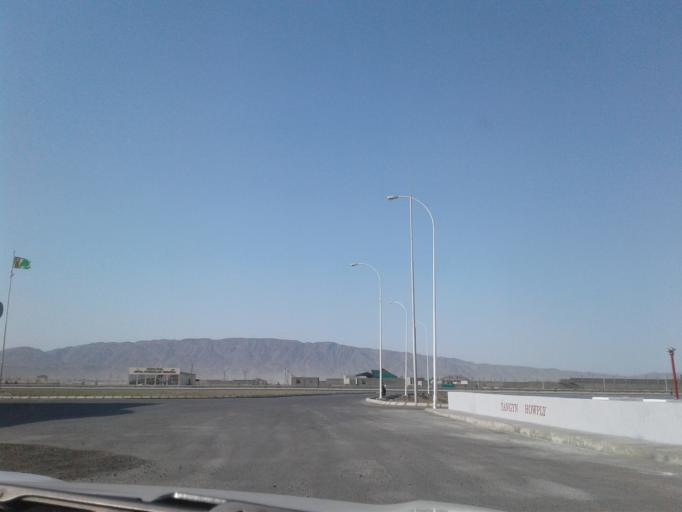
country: TM
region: Balkan
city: Serdar
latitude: 39.0062
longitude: 56.2530
